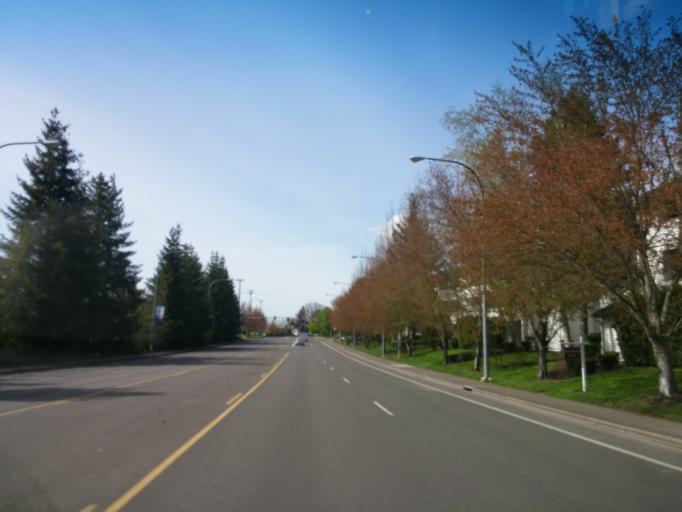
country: US
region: Oregon
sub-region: Washington County
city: Aloha
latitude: 45.5103
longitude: -122.8476
